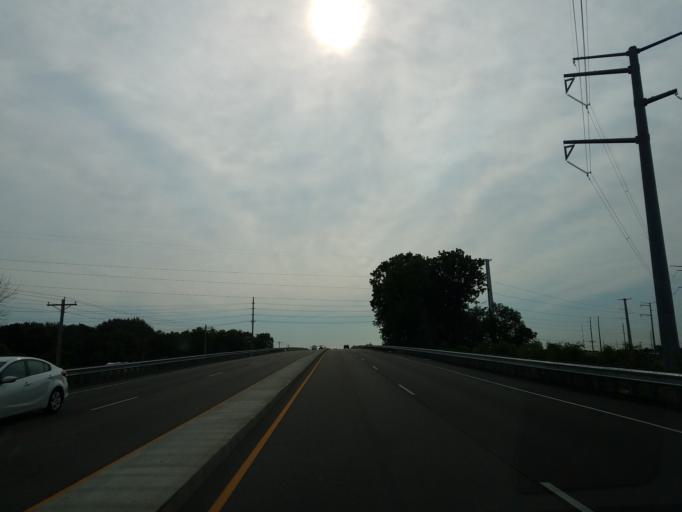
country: US
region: Illinois
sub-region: McLean County
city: Bloomington
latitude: 40.4593
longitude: -88.9854
